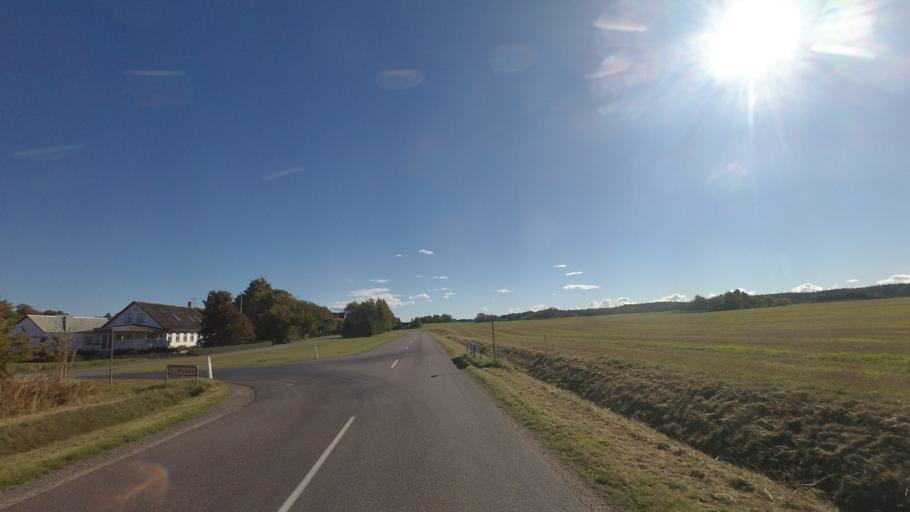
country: DK
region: Capital Region
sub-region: Bornholm Kommune
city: Nexo
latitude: 55.1099
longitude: 15.1110
